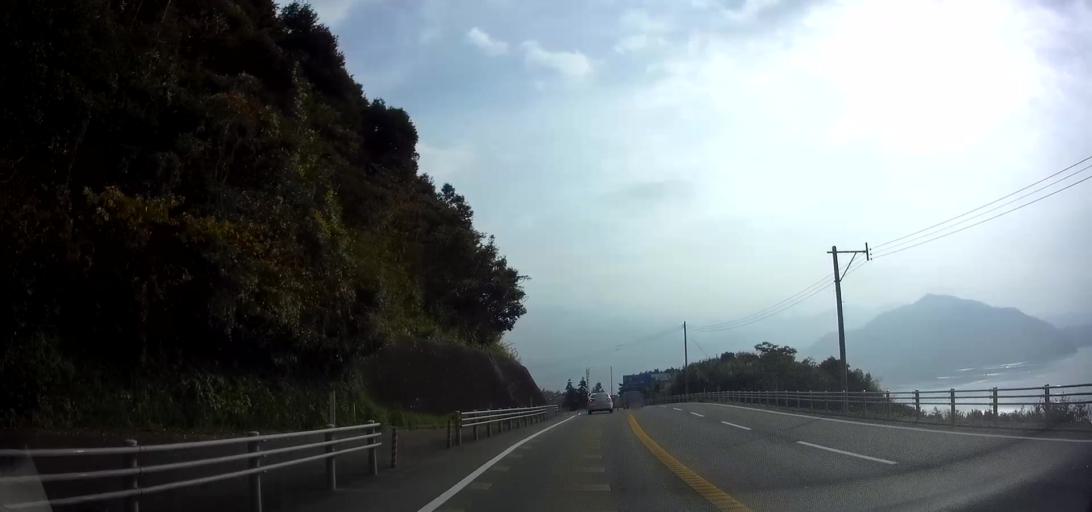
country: JP
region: Nagasaki
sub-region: Isahaya-shi
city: Isahaya
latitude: 32.7961
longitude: 130.1737
